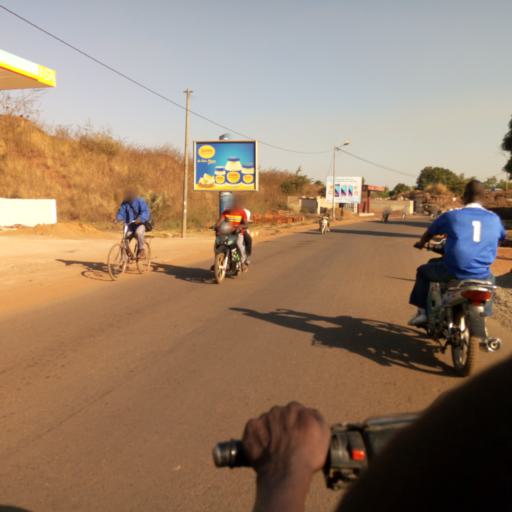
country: ML
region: Bamako
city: Bamako
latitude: 12.6597
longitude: -8.0330
